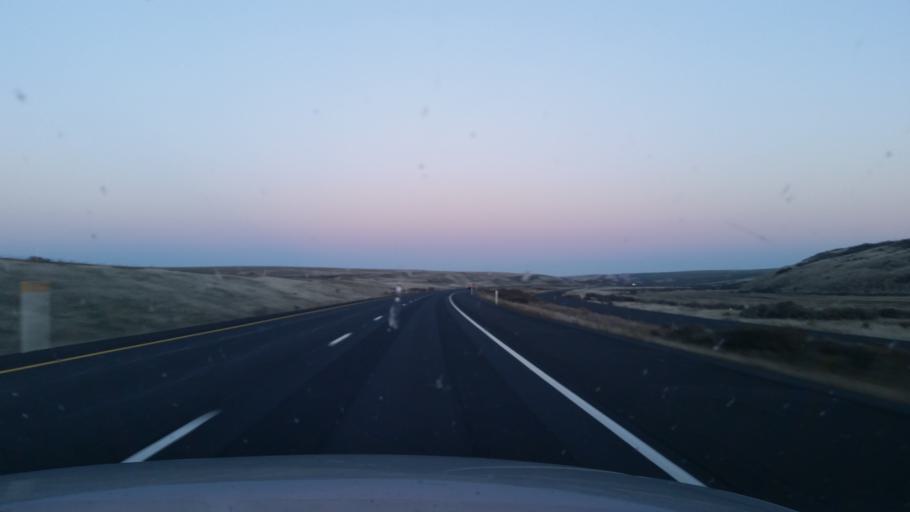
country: US
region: Washington
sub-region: Adams County
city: Ritzville
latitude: 47.1103
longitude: -118.5746
